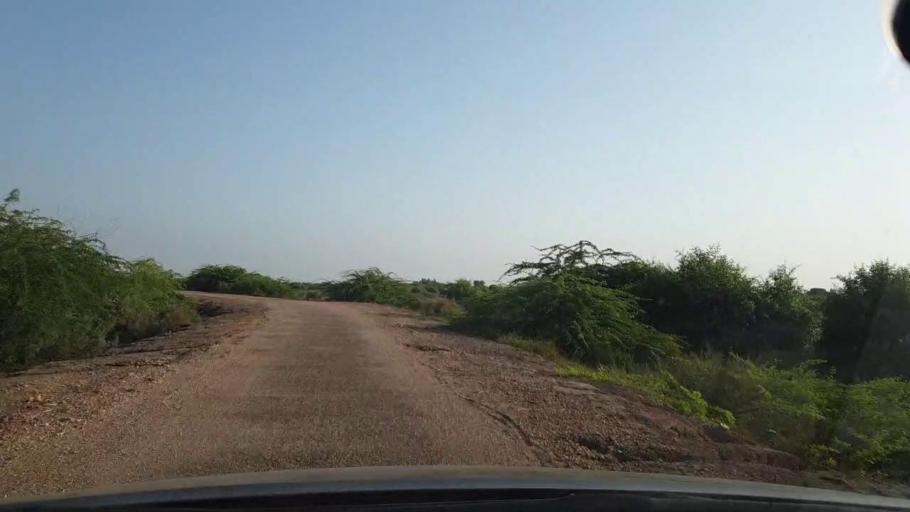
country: PK
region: Sindh
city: Naukot
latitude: 24.8178
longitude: 69.2002
